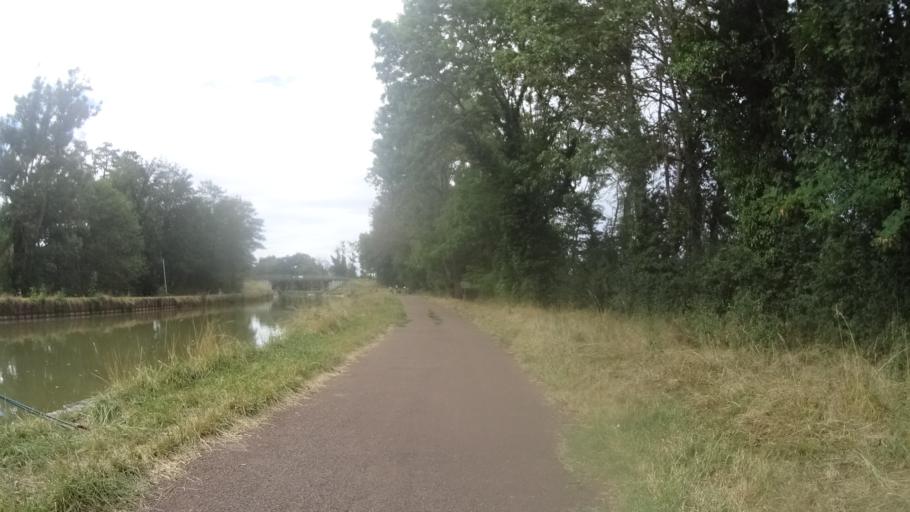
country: FR
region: Bourgogne
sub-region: Departement de la Nievre
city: Imphy
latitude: 46.9250
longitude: 3.2367
